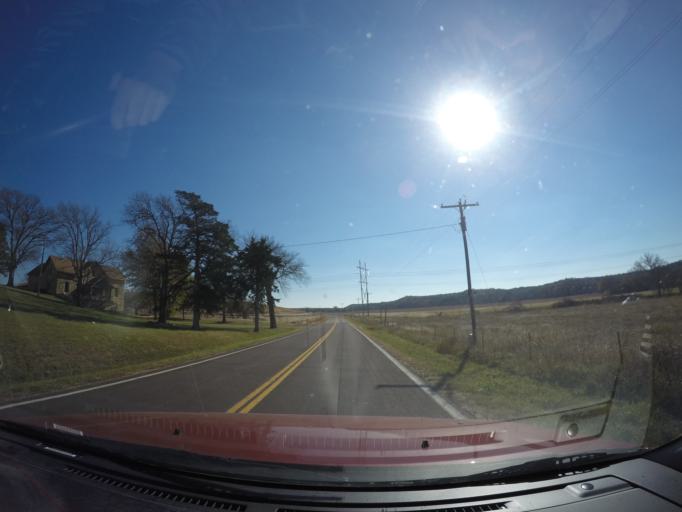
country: US
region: Kansas
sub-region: Geary County
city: Grandview Plaza
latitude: 38.9852
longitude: -96.7231
